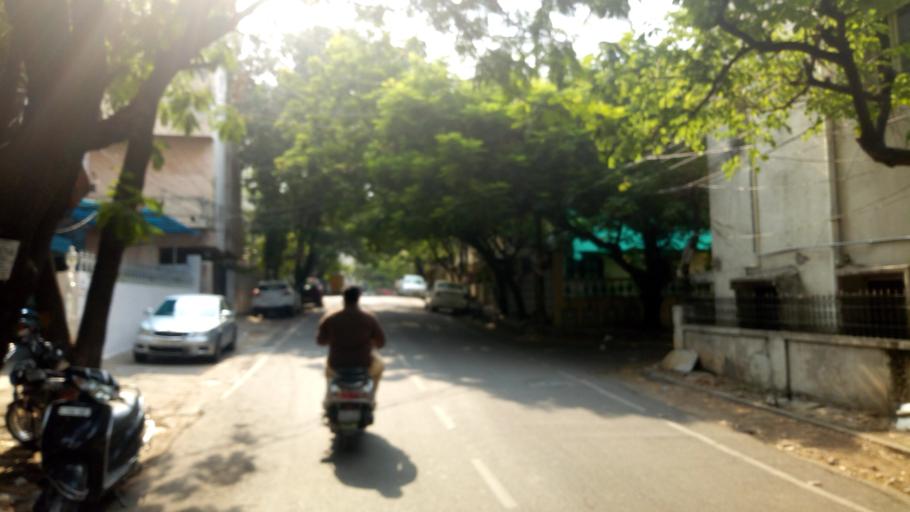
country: IN
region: Telangana
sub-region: Hyderabad
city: Hyderabad
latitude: 17.4059
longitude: 78.4749
